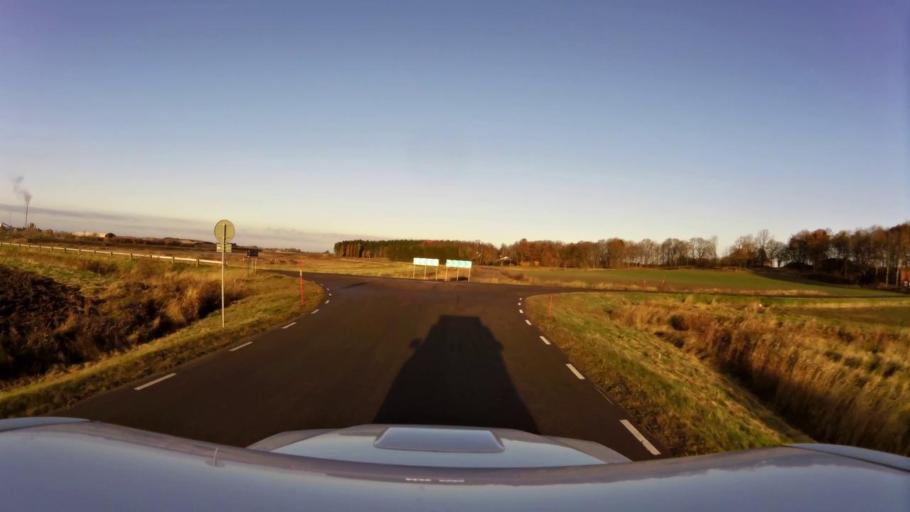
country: SE
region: OEstergoetland
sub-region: Linkopings Kommun
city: Ekangen
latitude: 58.4399
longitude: 15.6746
